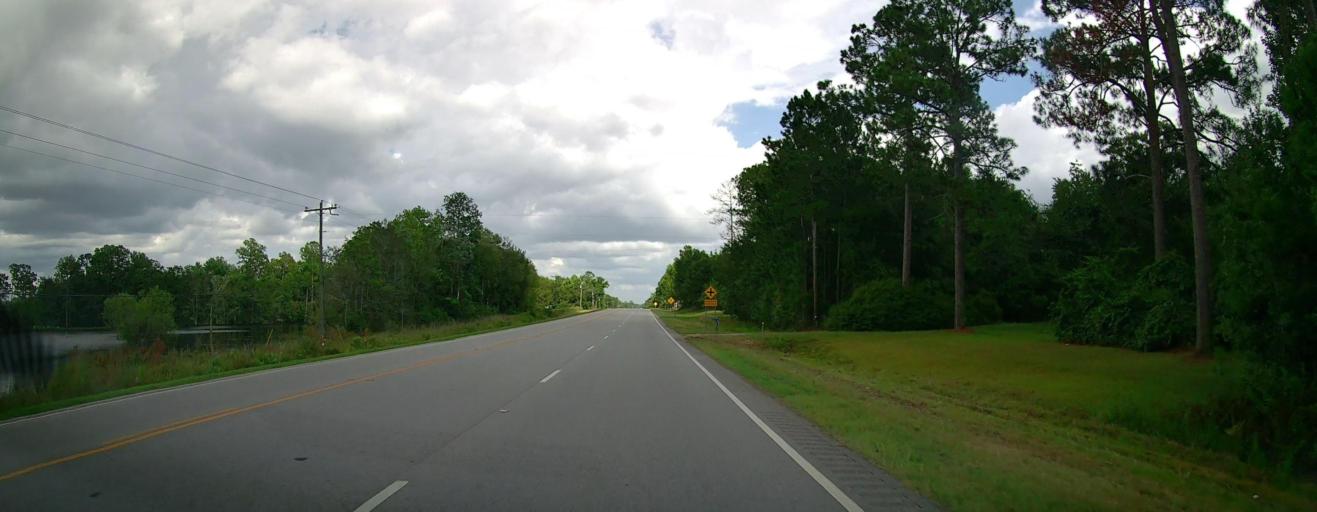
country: US
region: Georgia
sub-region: Coffee County
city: Broxton
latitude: 31.5658
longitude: -83.0042
